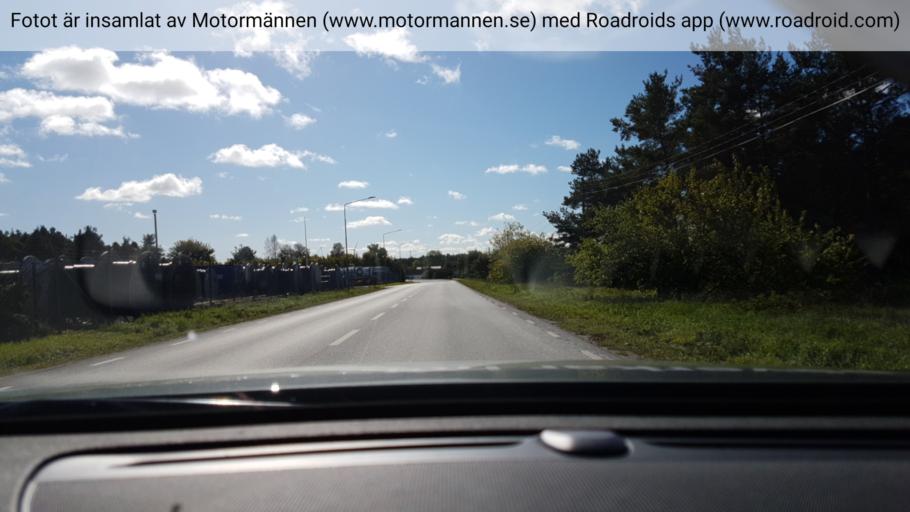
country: SE
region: Gotland
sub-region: Gotland
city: Slite
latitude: 57.7255
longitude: 18.7889
